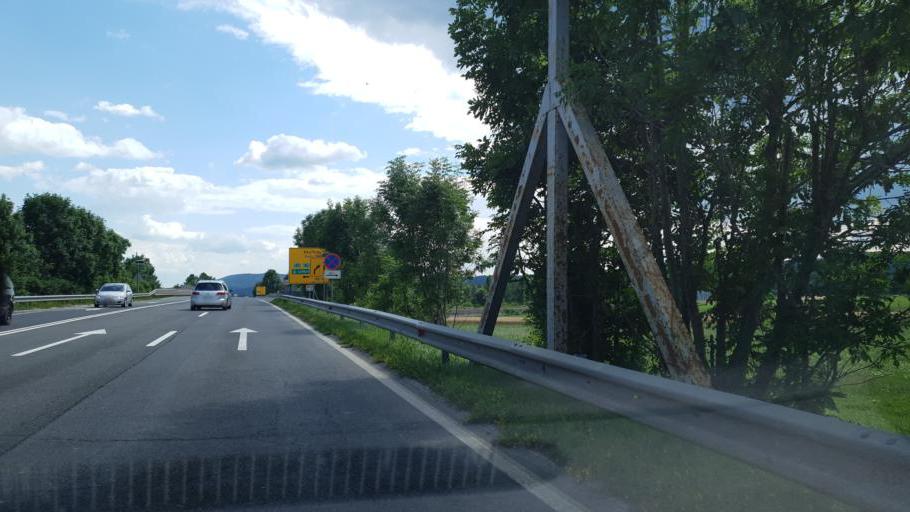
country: SI
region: Postojna
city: Postojna
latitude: 45.7615
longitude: 14.1956
